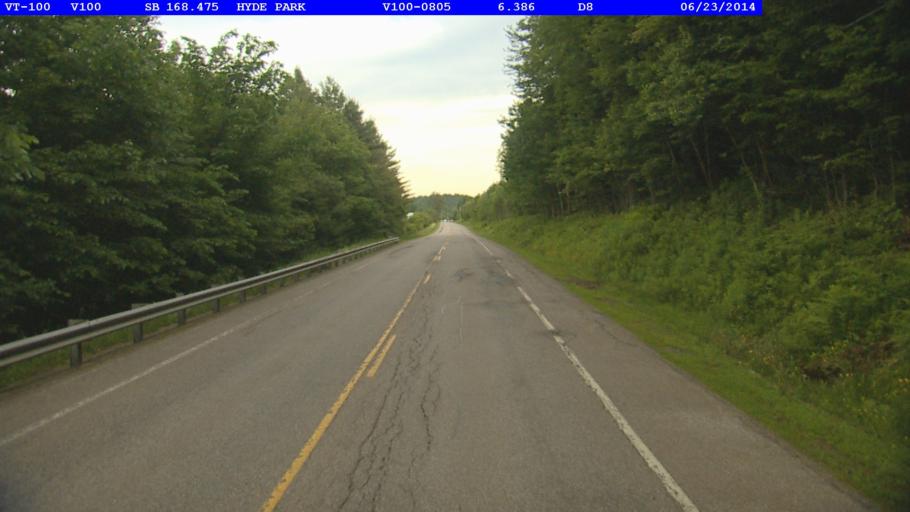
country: US
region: Vermont
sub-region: Lamoille County
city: Hyde Park
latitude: 44.6820
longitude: -72.5921
